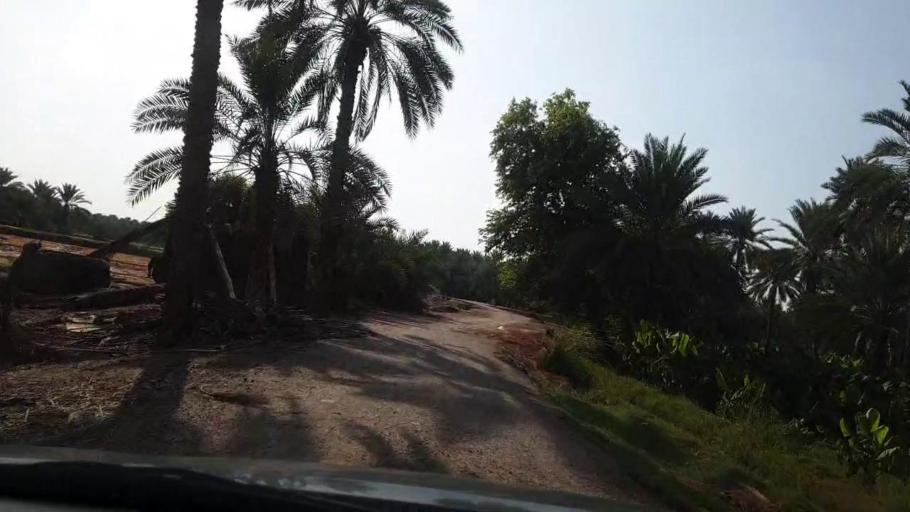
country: PK
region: Sindh
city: Sukkur
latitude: 27.6421
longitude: 68.8212
